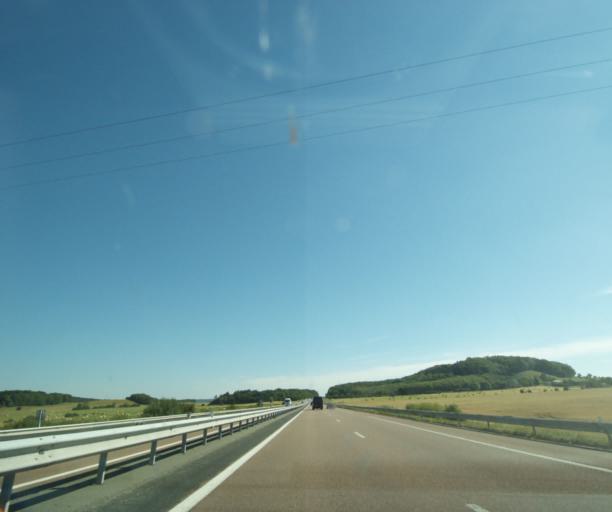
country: FR
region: Champagne-Ardenne
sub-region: Departement de la Haute-Marne
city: Saulxures
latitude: 48.0546
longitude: 5.5800
